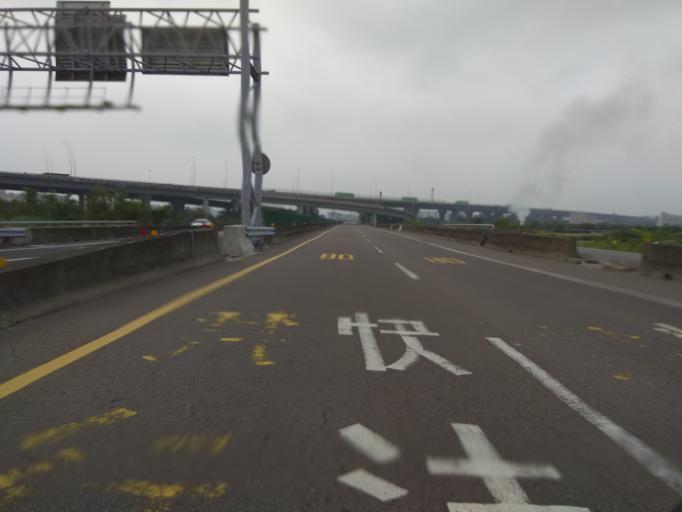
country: TW
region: Taiwan
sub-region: Hsinchu
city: Hsinchu
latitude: 24.7038
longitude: 120.8672
